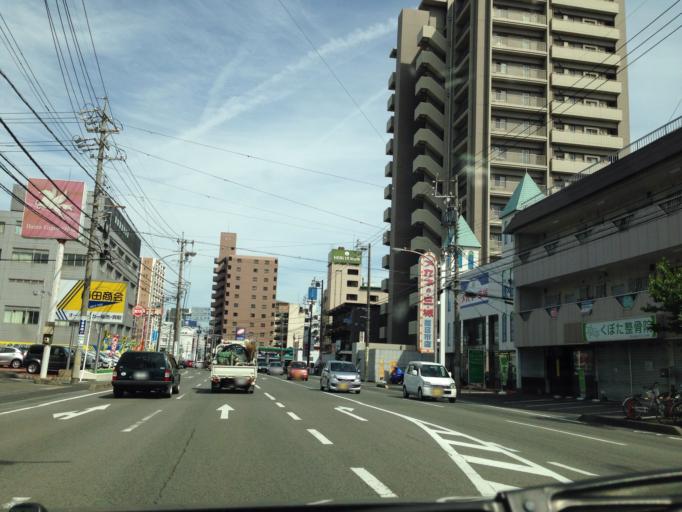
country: JP
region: Mie
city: Yokkaichi
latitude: 34.9734
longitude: 136.6111
